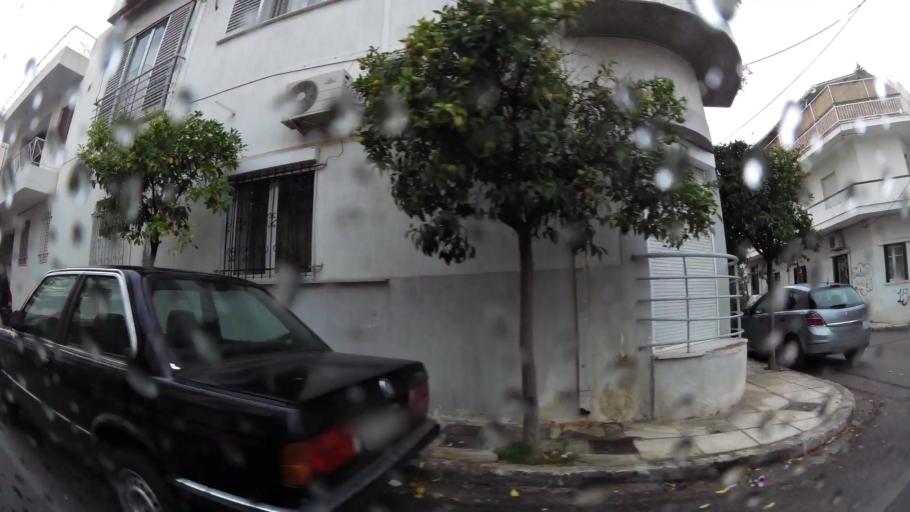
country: GR
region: Attica
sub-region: Nomarchia Athinas
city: Vyronas
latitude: 37.9554
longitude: 23.7573
